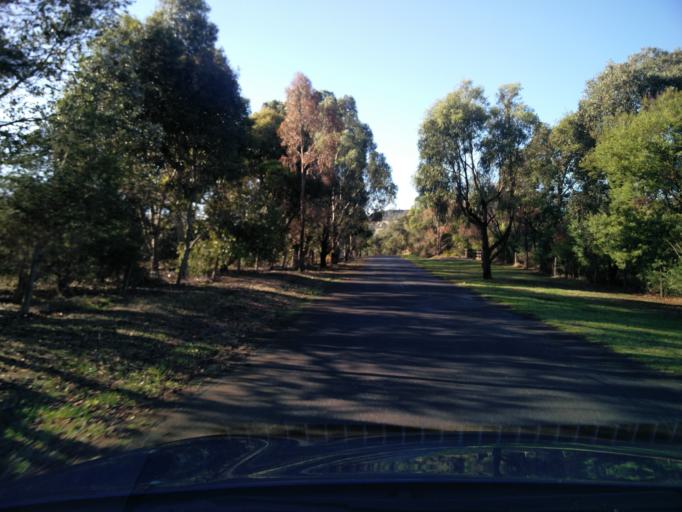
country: AU
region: Victoria
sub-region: Nillumbik
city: Wattleglen
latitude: -37.6823
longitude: 145.2051
